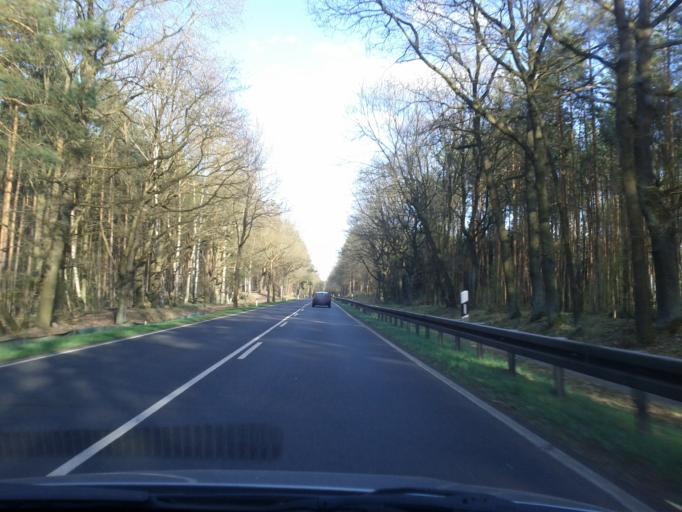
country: DE
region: Brandenburg
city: Spreenhagen
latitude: 52.3871
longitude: 13.9528
